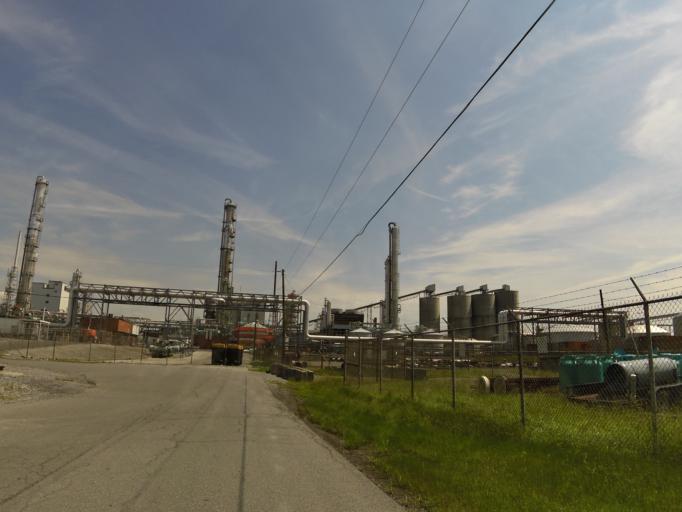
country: US
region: Tennessee
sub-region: Sullivan County
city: Kingsport
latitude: 36.5173
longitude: -82.5477
